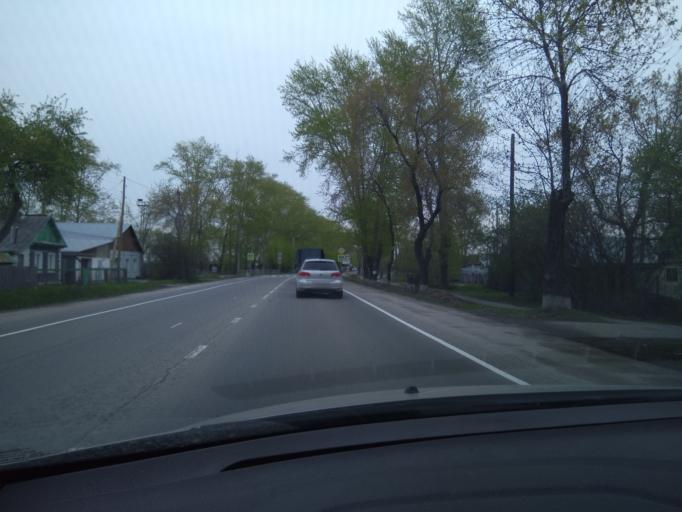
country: RU
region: Sverdlovsk
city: Bogdanovich
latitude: 56.7666
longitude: 62.0570
